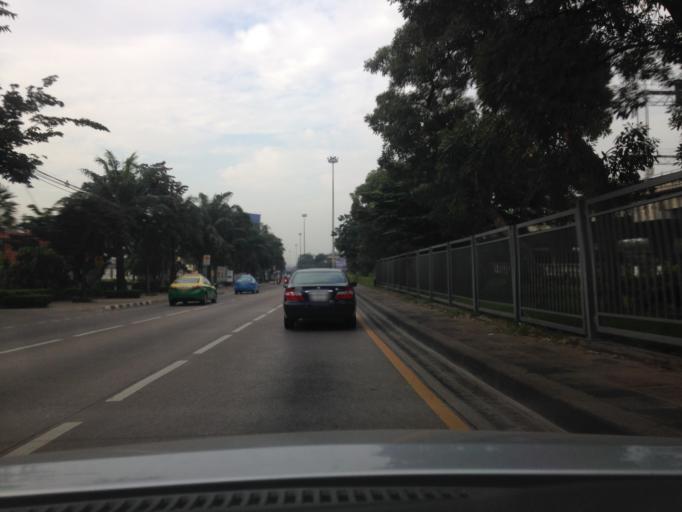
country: TH
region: Bangkok
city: Lat Phrao
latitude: 13.8172
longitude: 100.6243
